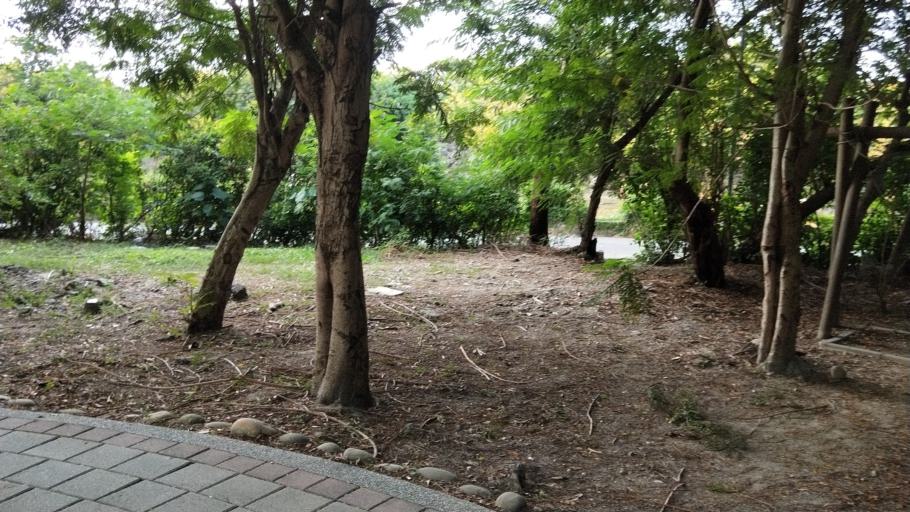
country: TW
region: Kaohsiung
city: Kaohsiung
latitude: 22.6792
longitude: 120.3010
